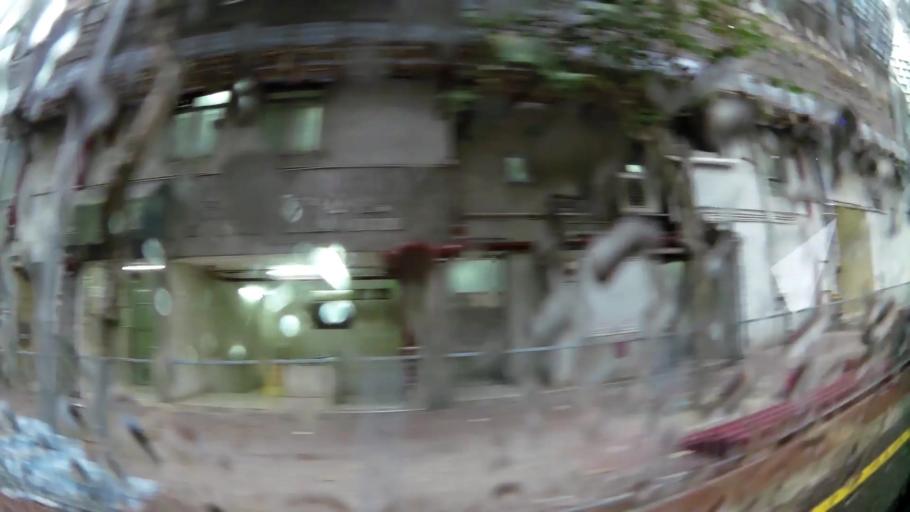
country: HK
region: Tsuen Wan
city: Tsuen Wan
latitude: 22.3708
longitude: 114.1214
